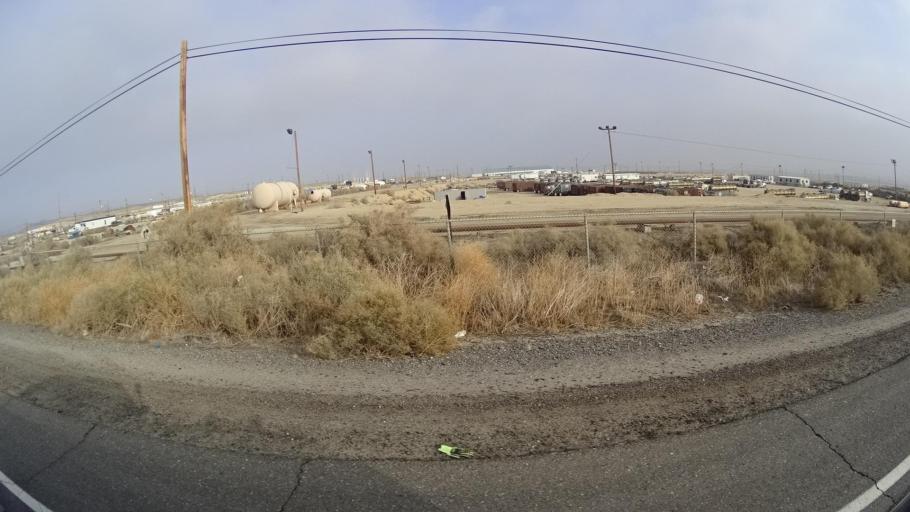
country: US
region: California
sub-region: Kern County
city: Ford City
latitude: 35.2339
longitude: -119.4457
